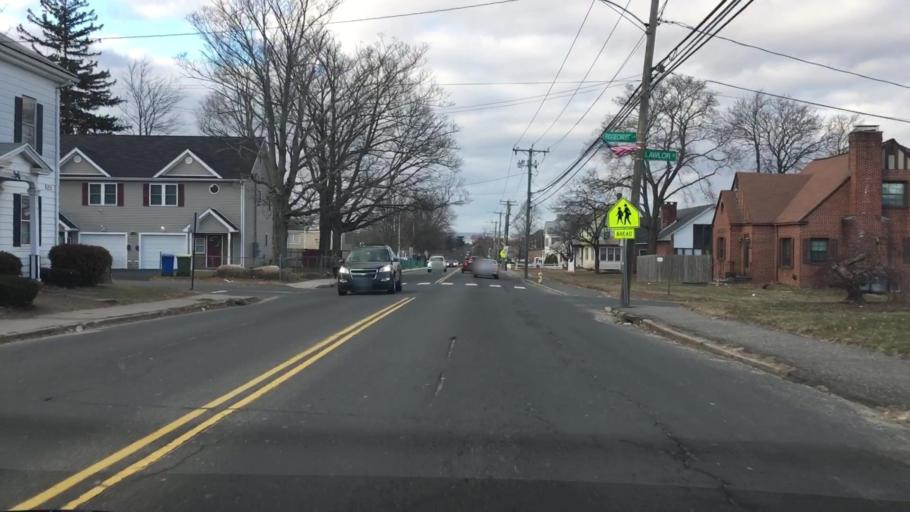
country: US
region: Connecticut
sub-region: New Haven County
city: Waterbury
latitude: 41.5446
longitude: -73.0555
